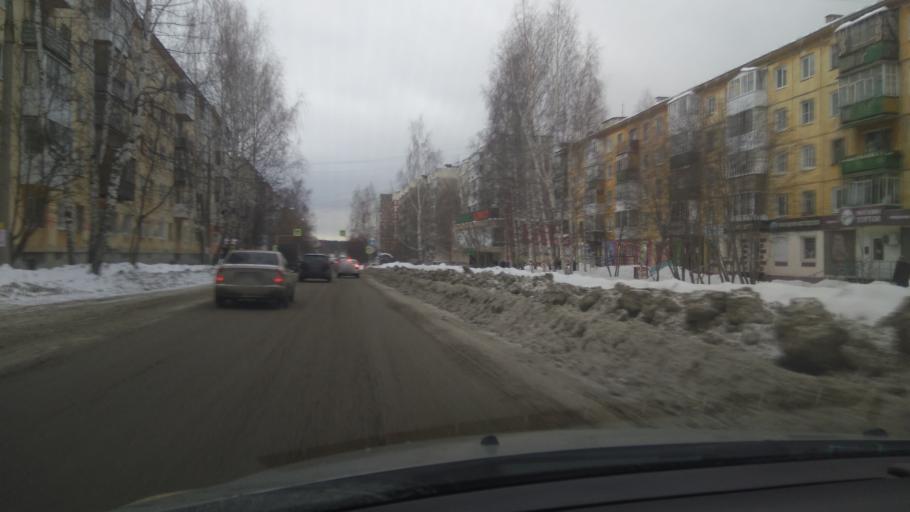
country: RU
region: Sverdlovsk
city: Verkhnyaya Pyshma
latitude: 56.9807
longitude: 60.5604
